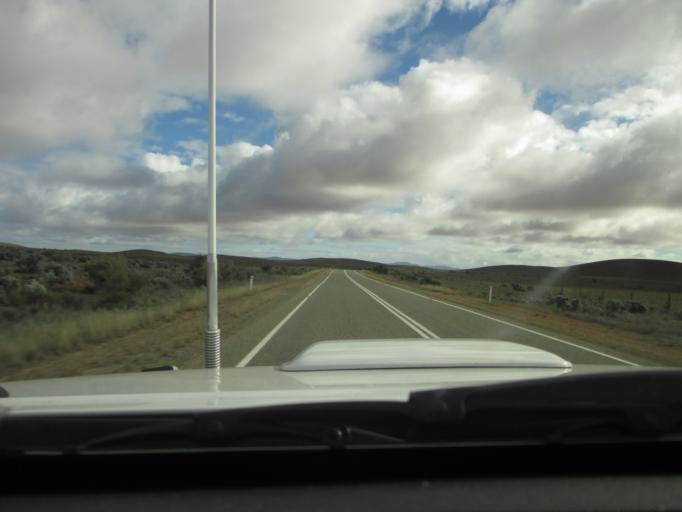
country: AU
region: South Australia
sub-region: Flinders Ranges
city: Quorn
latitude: -32.1584
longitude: 138.5295
